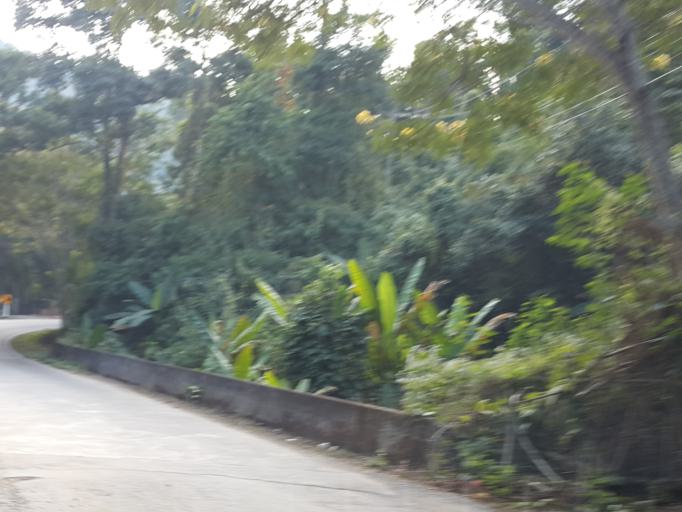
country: TH
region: Chiang Mai
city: Mae On
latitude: 18.8478
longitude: 99.2856
